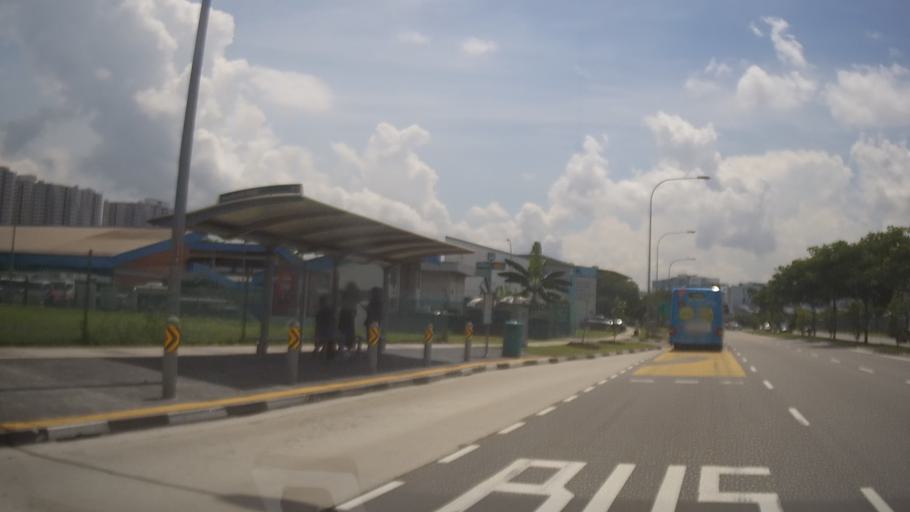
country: MY
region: Johor
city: Johor Bahru
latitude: 1.3963
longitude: 103.7543
